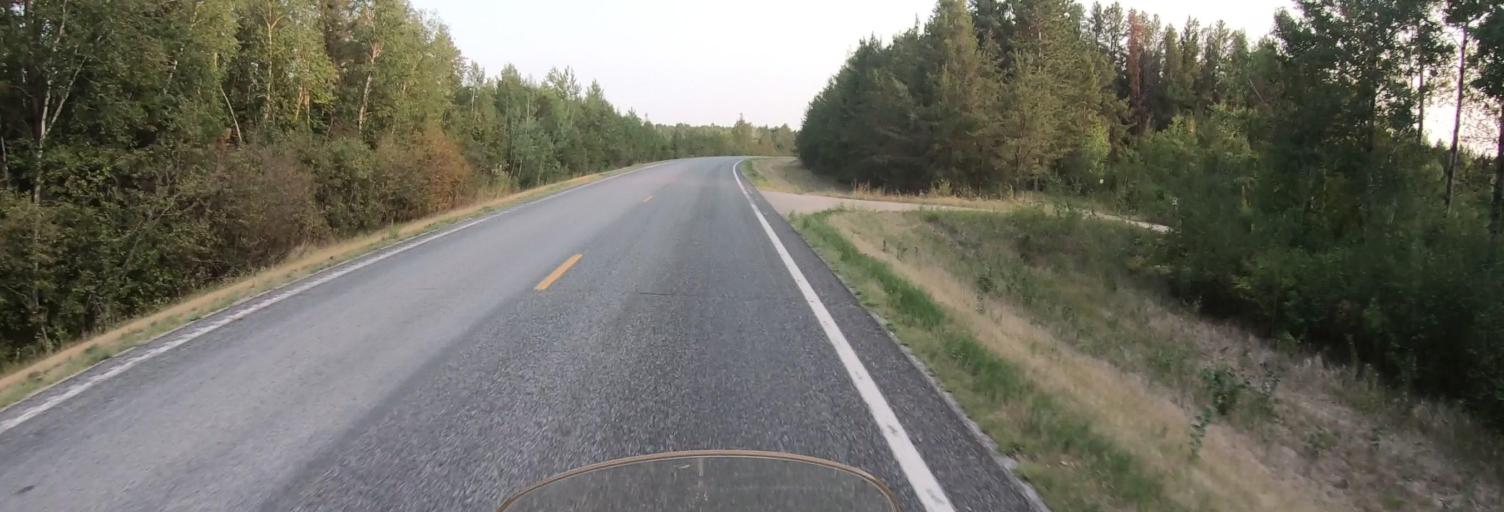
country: US
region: Minnesota
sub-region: Roseau County
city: Warroad
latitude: 48.7390
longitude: -95.3308
